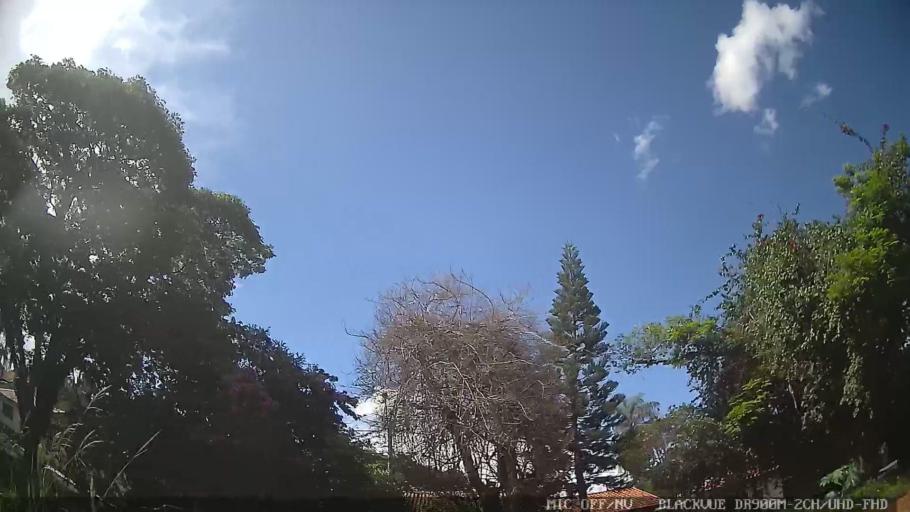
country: BR
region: Sao Paulo
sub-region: Pedreira
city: Pedreira
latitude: -22.7228
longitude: -46.8473
